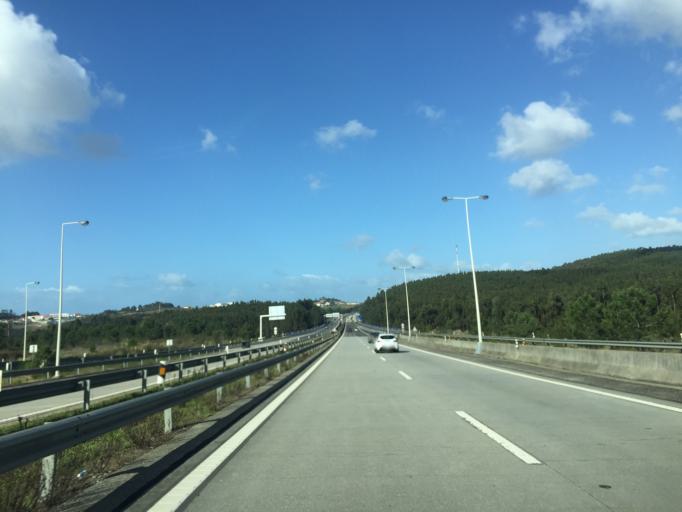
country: PT
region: Lisbon
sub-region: Torres Vedras
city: Torres Vedras
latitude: 39.1113
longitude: -9.2445
